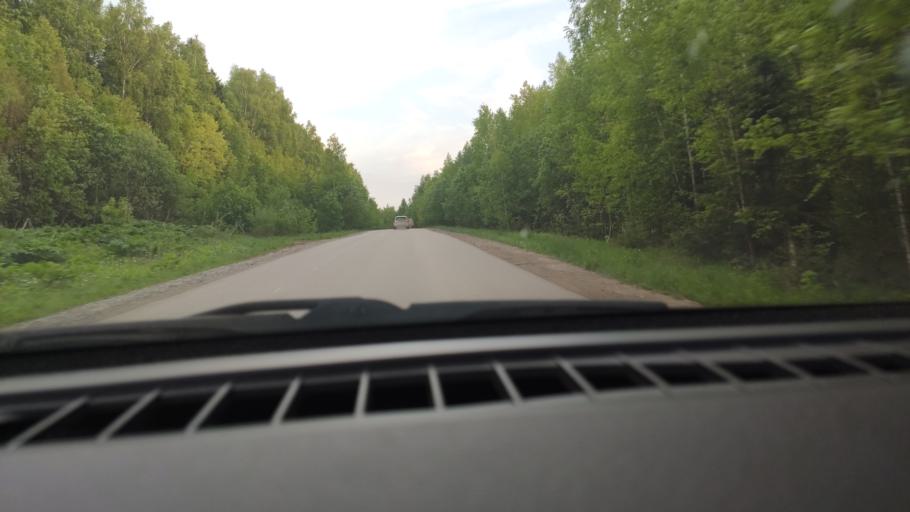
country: RU
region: Perm
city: Kondratovo
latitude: 58.0657
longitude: 56.0021
